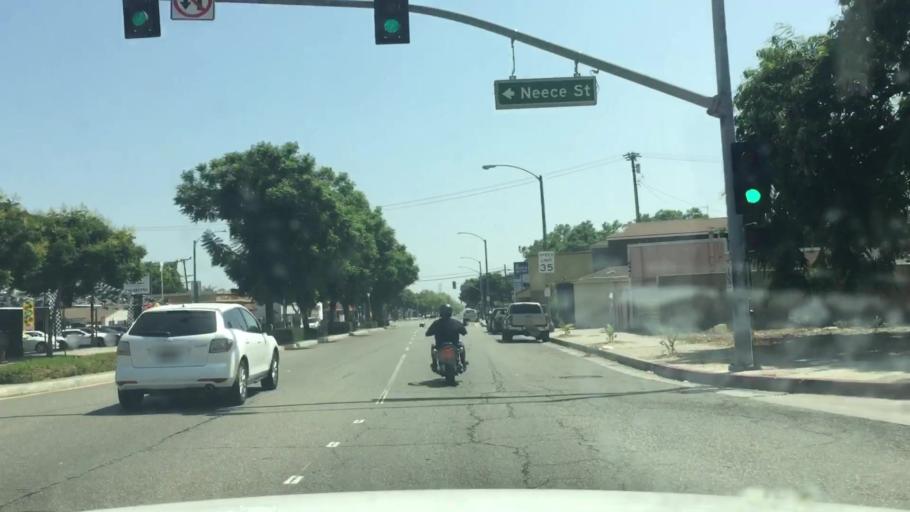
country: US
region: California
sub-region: Los Angeles County
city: East Rancho Dominguez
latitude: 33.8719
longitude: -118.2022
